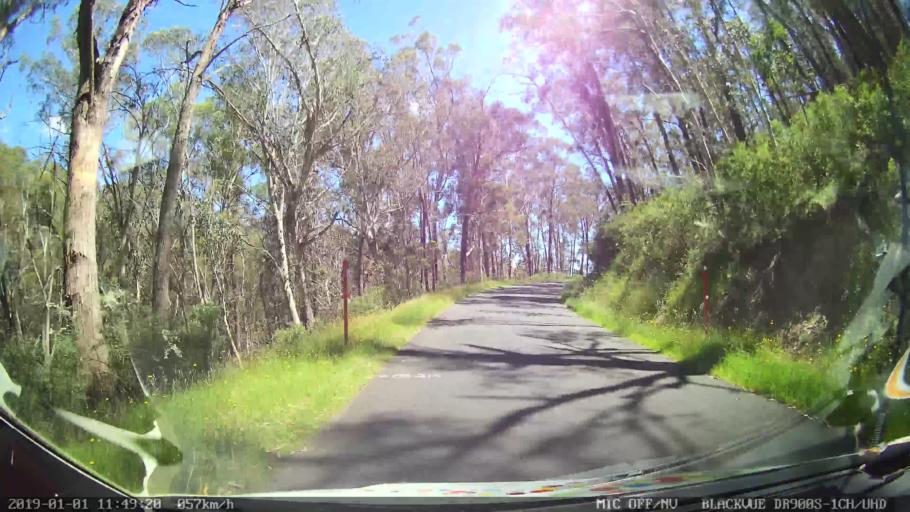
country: AU
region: New South Wales
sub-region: Snowy River
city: Jindabyne
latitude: -35.8945
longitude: 148.4134
